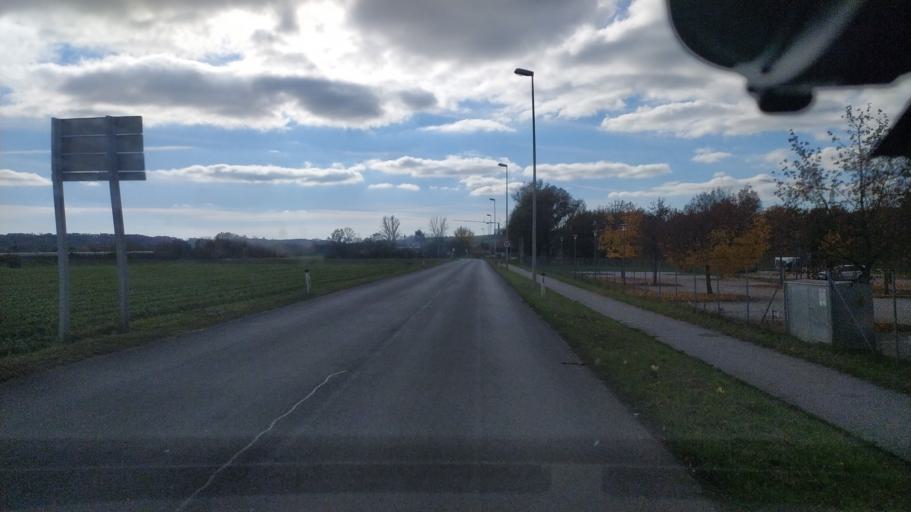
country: AT
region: Upper Austria
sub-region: Politischer Bezirk Urfahr-Umgebung
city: Steyregg
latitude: 48.2486
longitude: 14.3823
